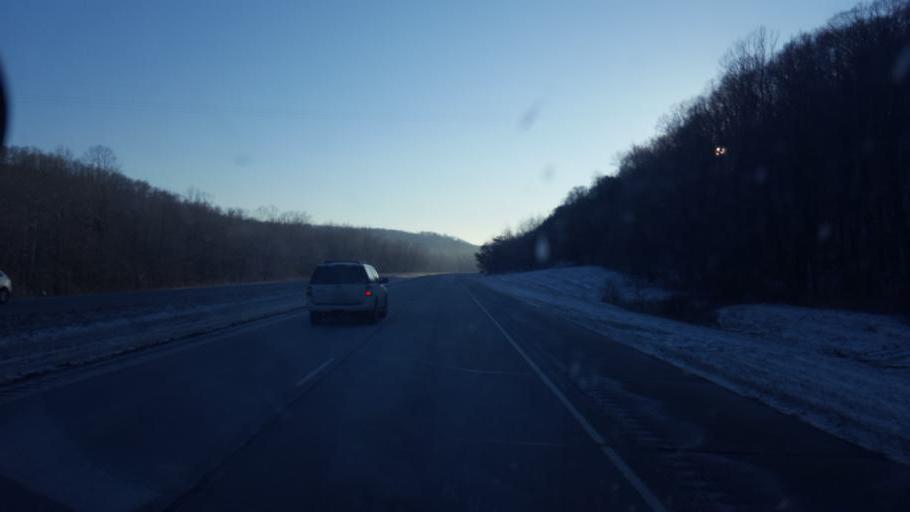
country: US
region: Ohio
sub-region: Pike County
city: Piketon
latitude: 39.0605
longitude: -83.0777
